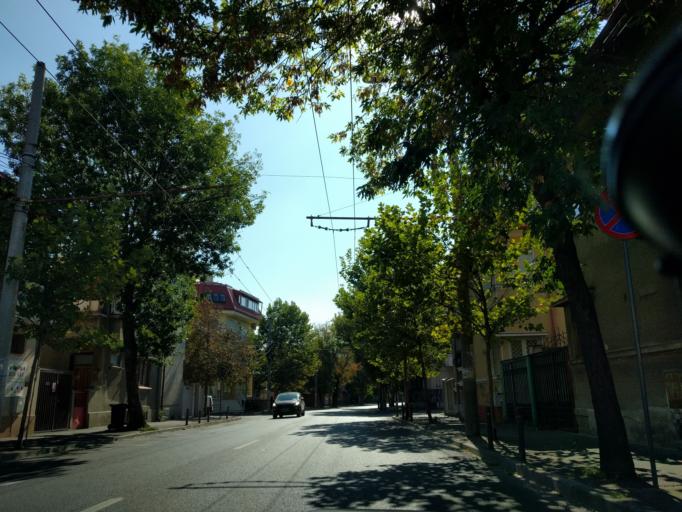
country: RO
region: Bucuresti
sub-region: Municipiul Bucuresti
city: Bucharest
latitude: 44.4266
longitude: 26.1351
